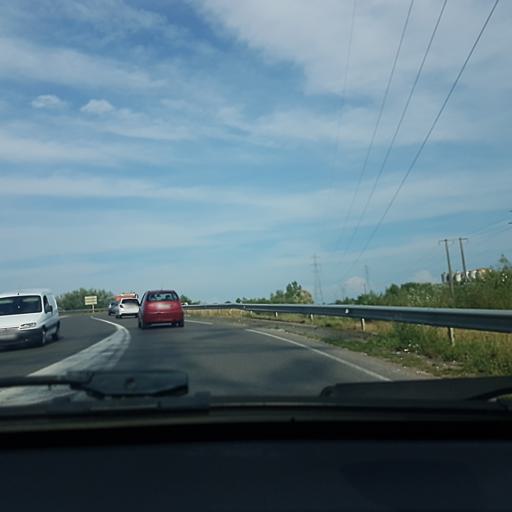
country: FR
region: Bourgogne
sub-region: Departement de Saone-et-Loire
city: Saint-Marcel
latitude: 46.7618
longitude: 4.8718
